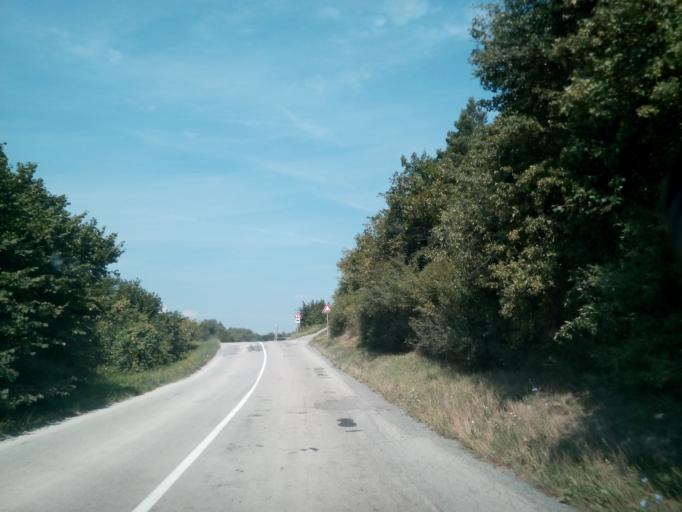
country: SK
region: Kosicky
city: Kosice
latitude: 48.8132
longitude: 21.2353
